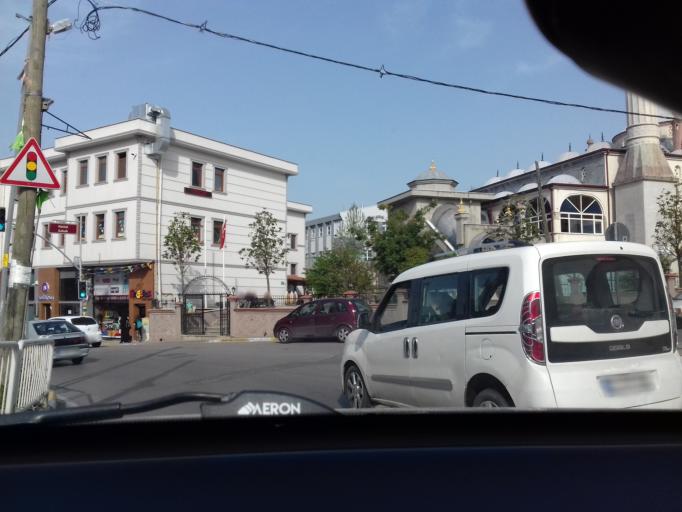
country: TR
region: Istanbul
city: Pendik
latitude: 40.9060
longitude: 29.2537
